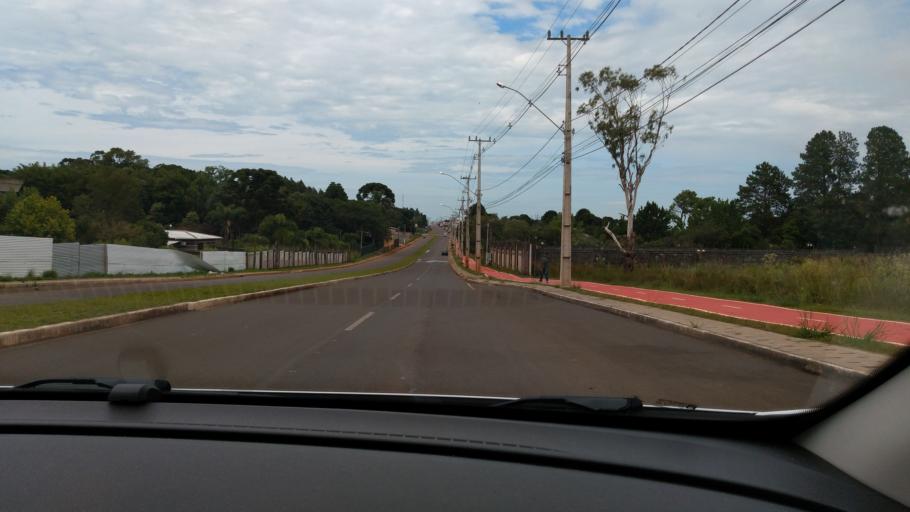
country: BR
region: Parana
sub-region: Guarapuava
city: Guarapuava
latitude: -25.3684
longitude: -51.4378
